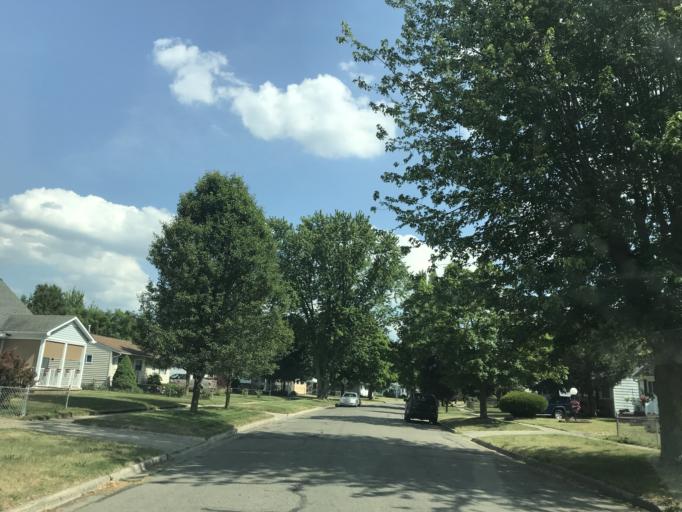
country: US
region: Michigan
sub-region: Washtenaw County
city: Ypsilanti
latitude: 42.2565
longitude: -83.5830
